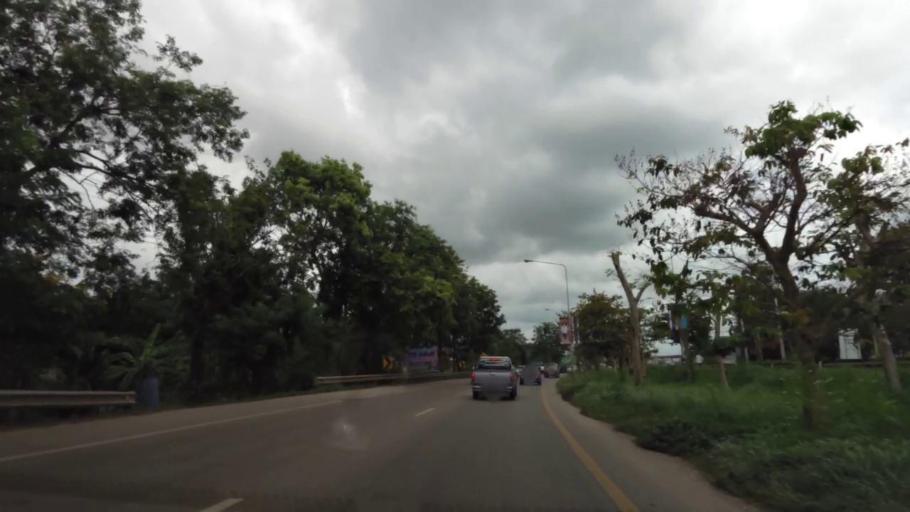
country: TH
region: Rayong
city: Klaeng
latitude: 12.7756
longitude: 101.7152
